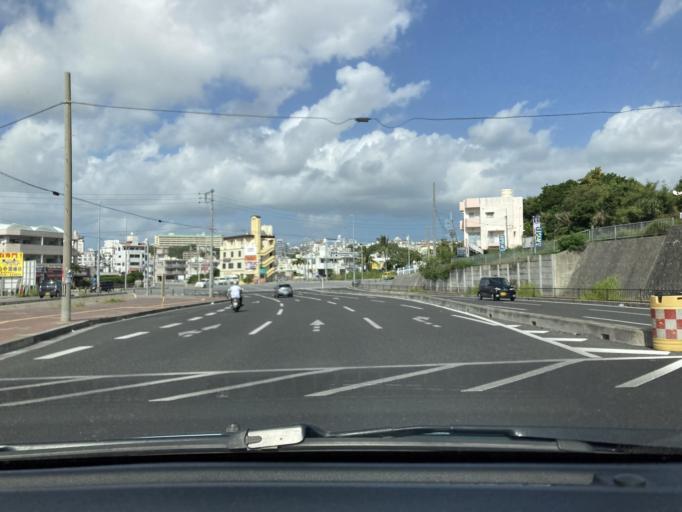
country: JP
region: Okinawa
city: Tomigusuku
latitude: 26.1929
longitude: 127.6946
